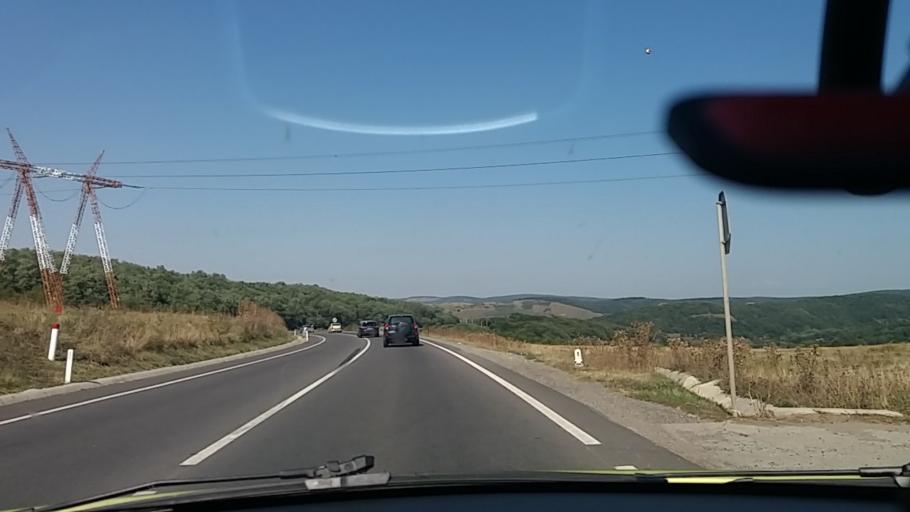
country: RO
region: Sibiu
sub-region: Comuna Sura Mare
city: Sura Mare
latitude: 45.8723
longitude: 24.1579
